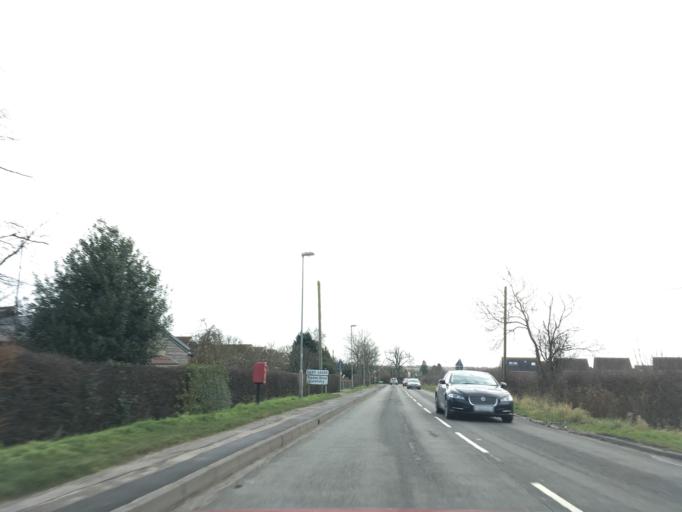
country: GB
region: England
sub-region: Nottinghamshire
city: East Leake
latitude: 52.8426
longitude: -1.1805
